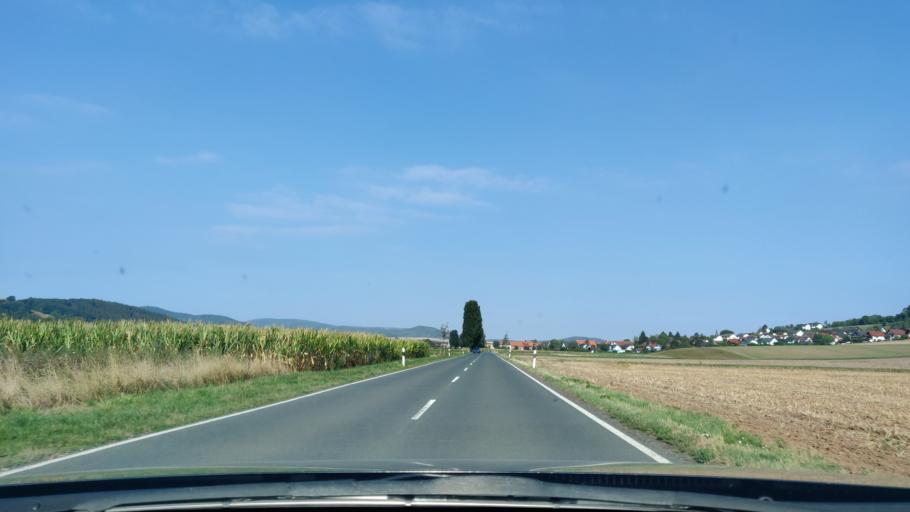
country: DE
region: Hesse
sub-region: Regierungsbezirk Kassel
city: Bad Wildungen
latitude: 51.1401
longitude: 9.1906
